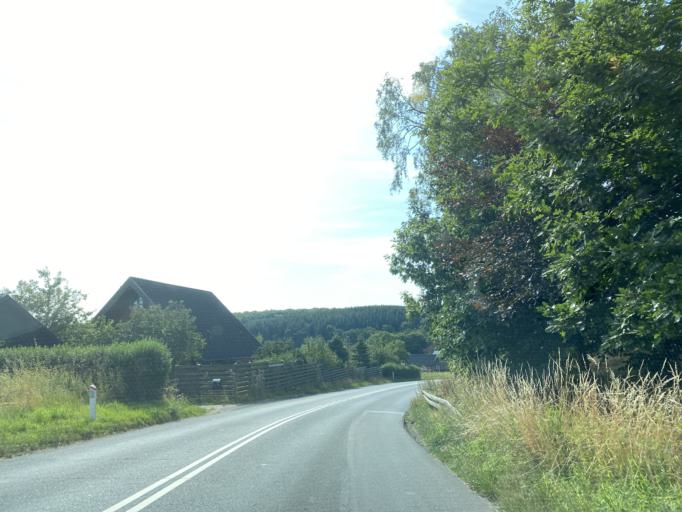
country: DK
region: Central Jutland
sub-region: Favrskov Kommune
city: Hammel
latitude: 56.2671
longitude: 9.8354
